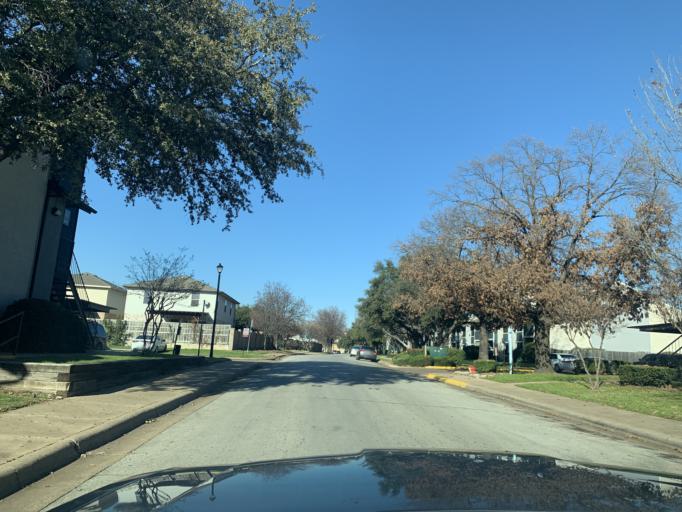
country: US
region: Texas
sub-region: Tarrant County
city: Bedford
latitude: 32.8334
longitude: -97.1395
